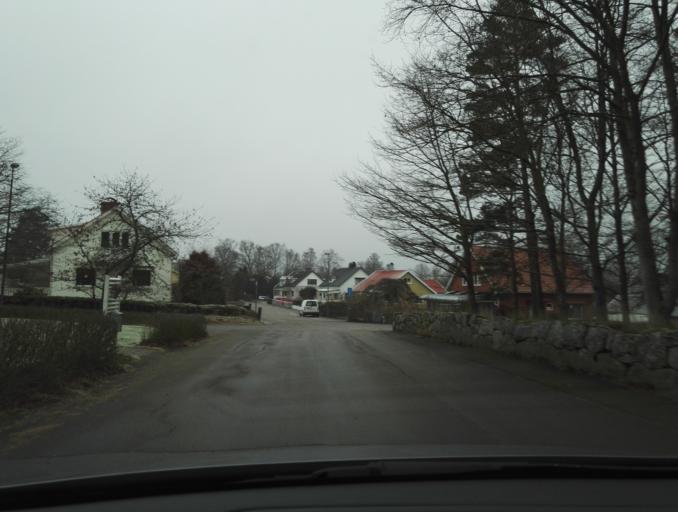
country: SE
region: Kronoberg
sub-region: Vaxjo Kommun
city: Vaexjoe
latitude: 56.9023
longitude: 14.7363
